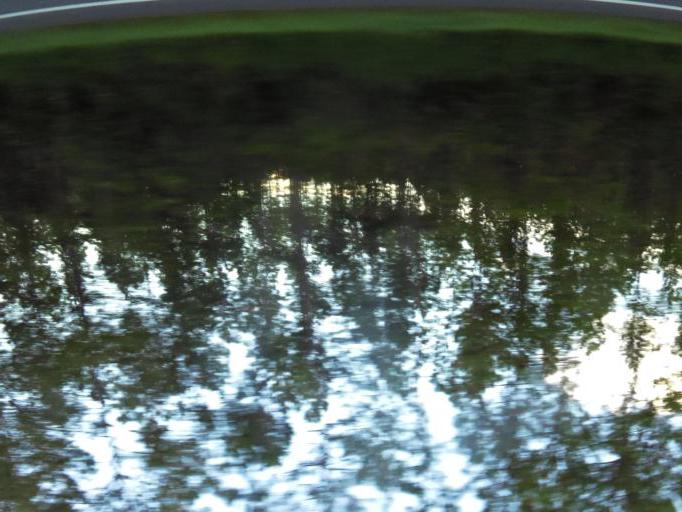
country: US
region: Georgia
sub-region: Echols County
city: Statenville
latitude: 30.7270
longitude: -83.0800
